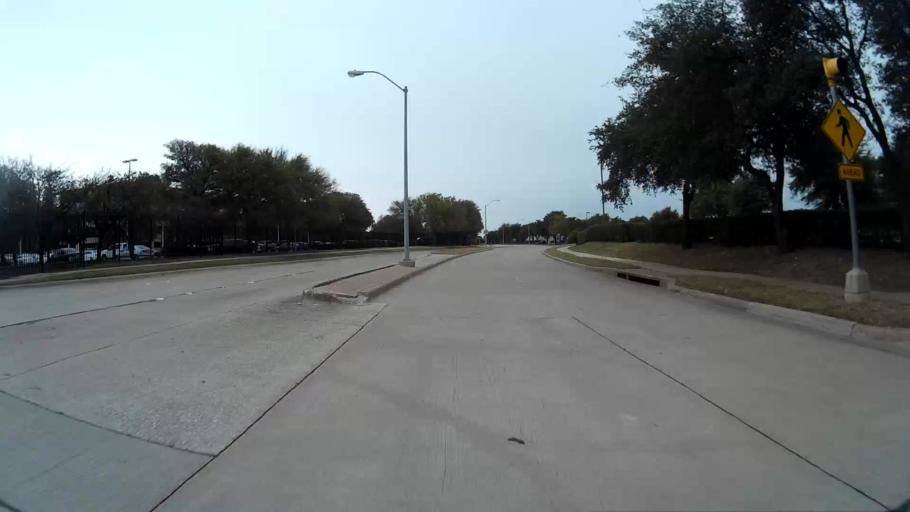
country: US
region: Texas
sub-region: Dallas County
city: Richardson
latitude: 32.9785
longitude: -96.7059
